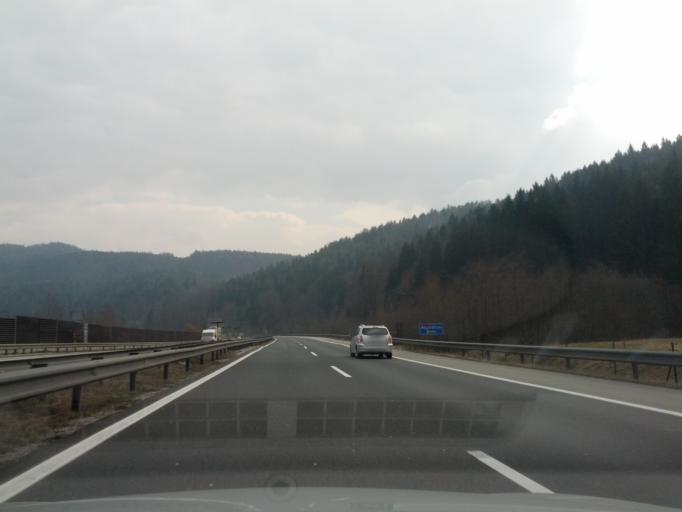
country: SI
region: Moravce
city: Moravce
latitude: 46.1675
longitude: 14.7390
